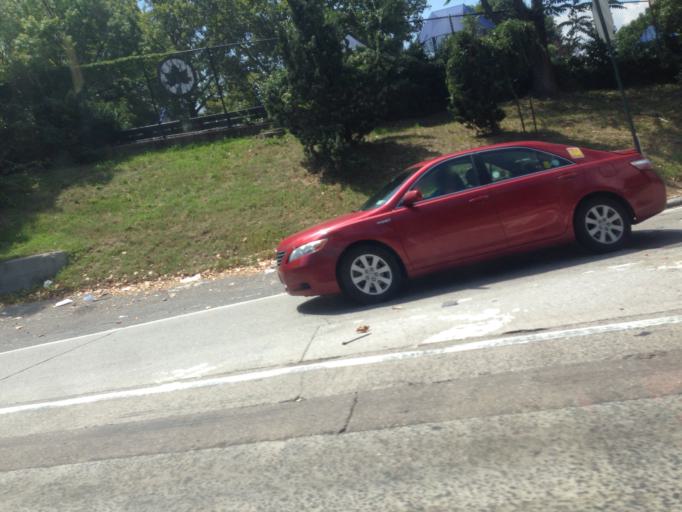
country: US
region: New York
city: New York City
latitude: 40.6899
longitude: -73.9988
